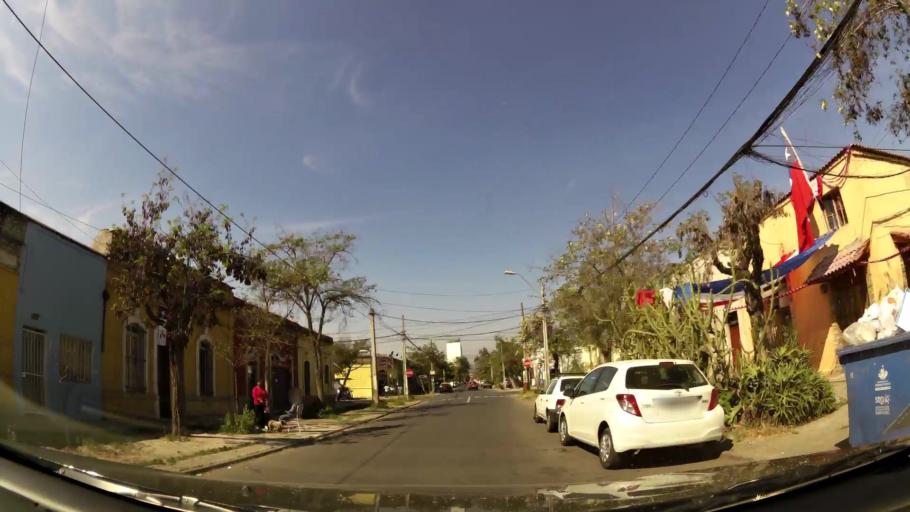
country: CL
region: Santiago Metropolitan
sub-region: Provincia de Santiago
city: Santiago
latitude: -33.4166
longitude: -70.6620
